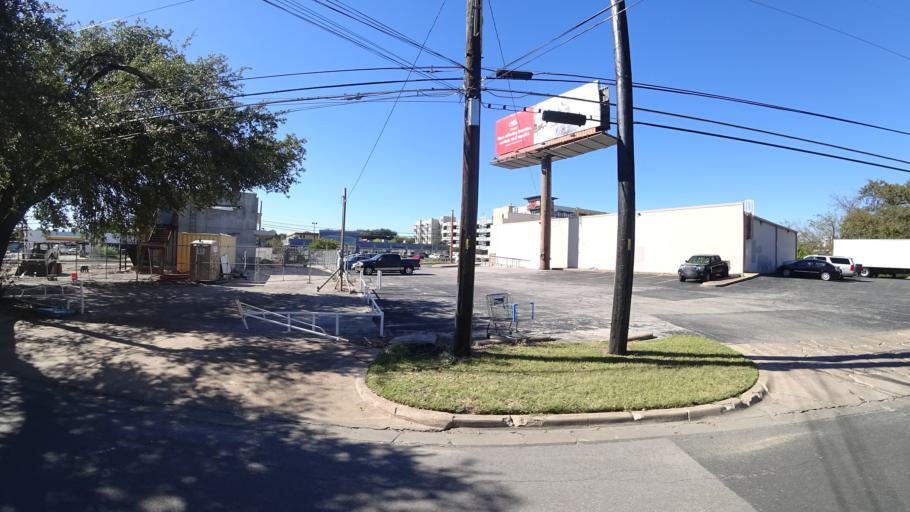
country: US
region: Texas
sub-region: Travis County
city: Austin
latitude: 30.3266
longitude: -97.7390
